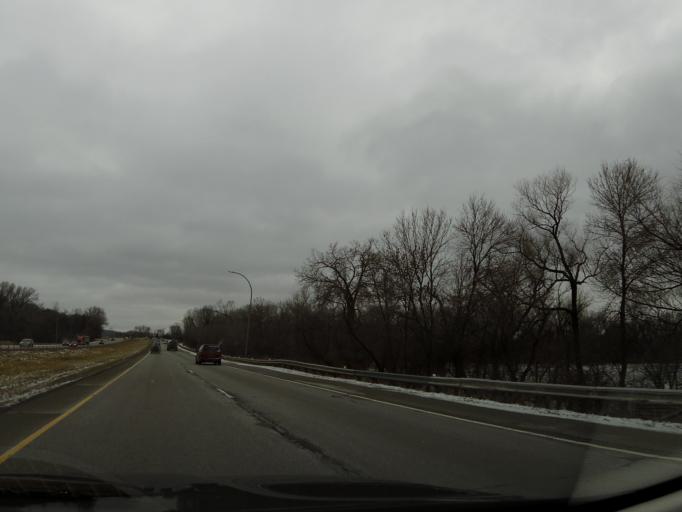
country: US
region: Minnesota
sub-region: Ramsey County
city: Maplewood
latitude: 44.9397
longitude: -93.0330
